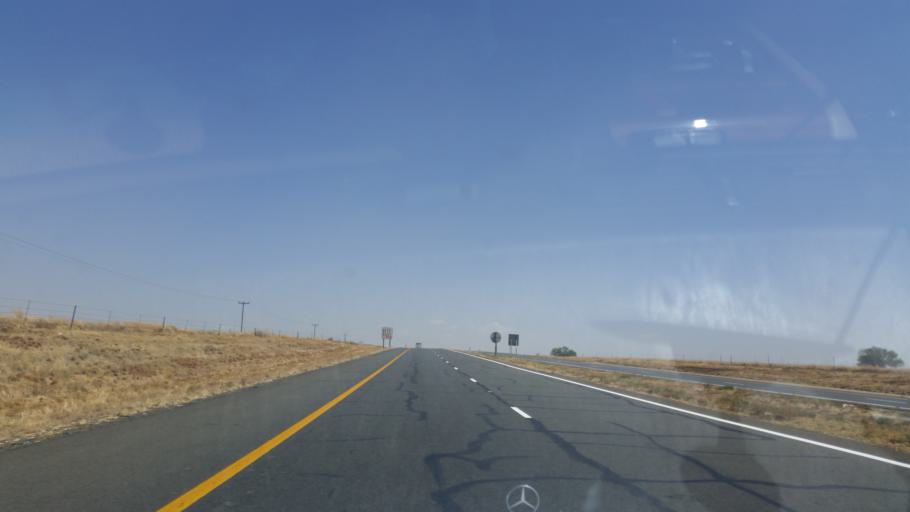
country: ZA
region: Orange Free State
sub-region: Lejweleputswa District Municipality
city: Brandfort
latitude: -28.8537
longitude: 26.5671
